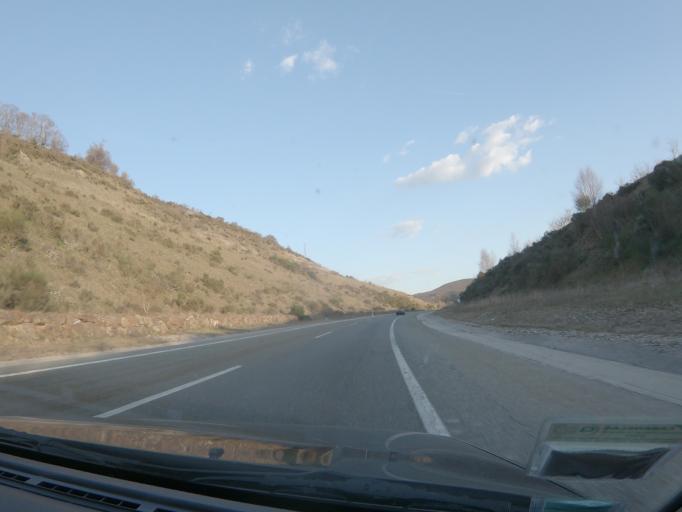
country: ES
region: Castille and Leon
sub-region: Provincia de Leon
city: Vega de Valcarce
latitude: 42.6743
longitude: -6.9616
